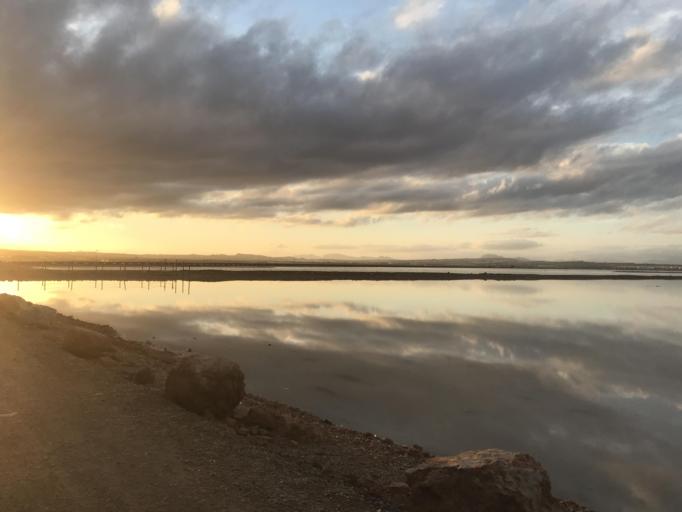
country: ES
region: Valencia
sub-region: Provincia de Alicante
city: Torrevieja
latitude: 37.9805
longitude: -0.7061
